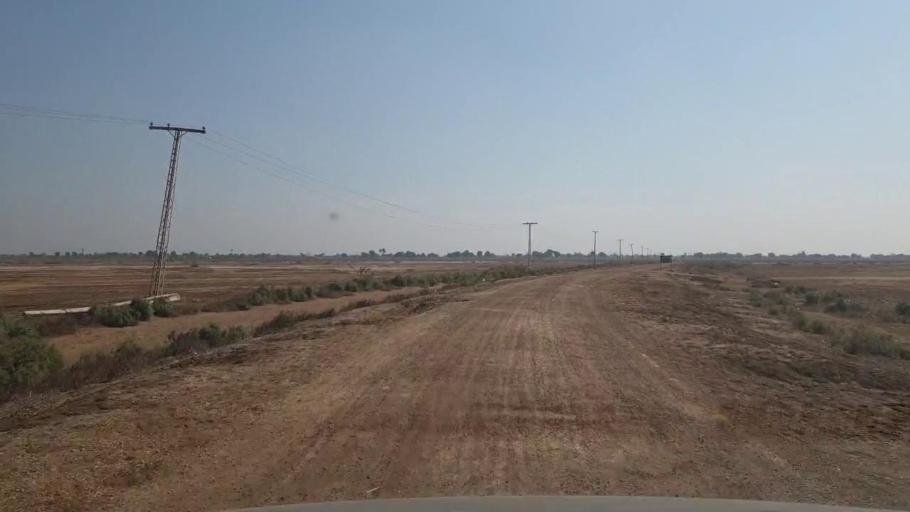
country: PK
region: Sindh
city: Digri
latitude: 25.2286
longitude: 69.2231
